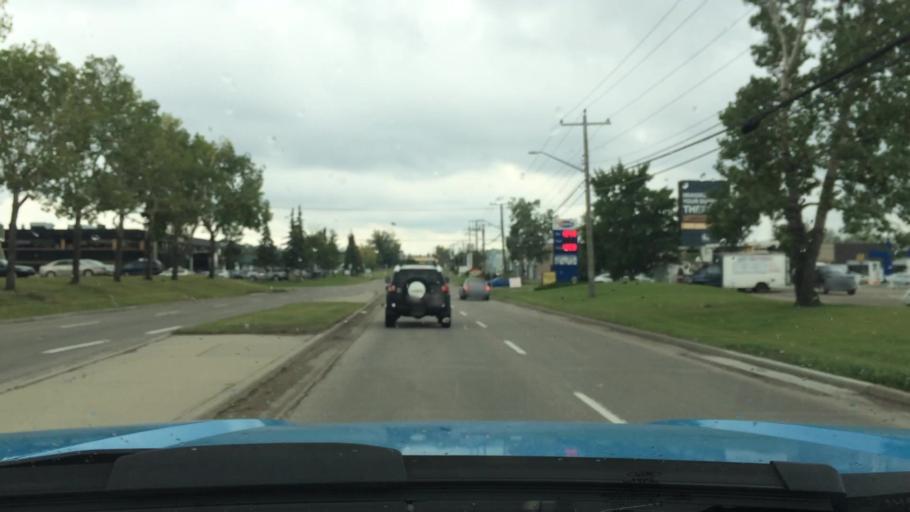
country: CA
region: Alberta
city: Calgary
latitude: 51.0807
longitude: -114.0117
